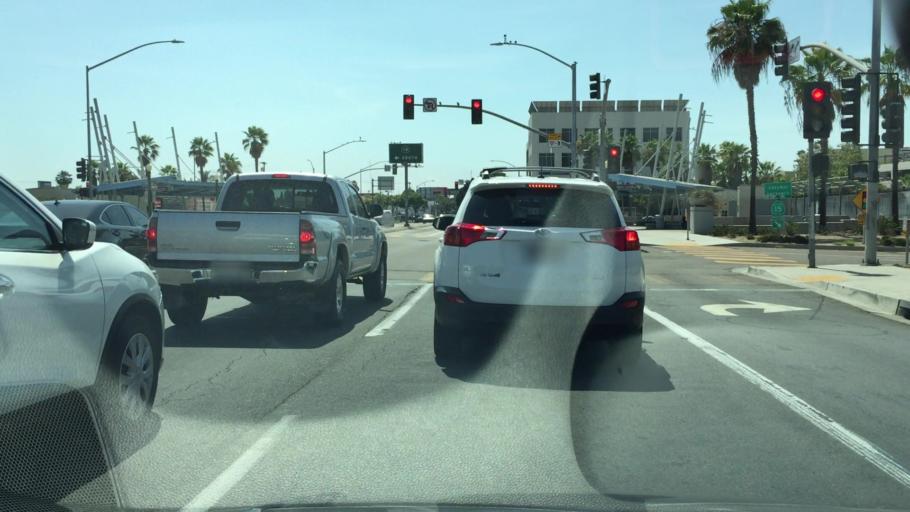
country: US
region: California
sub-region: San Diego County
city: San Diego
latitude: 32.7498
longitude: -117.1080
